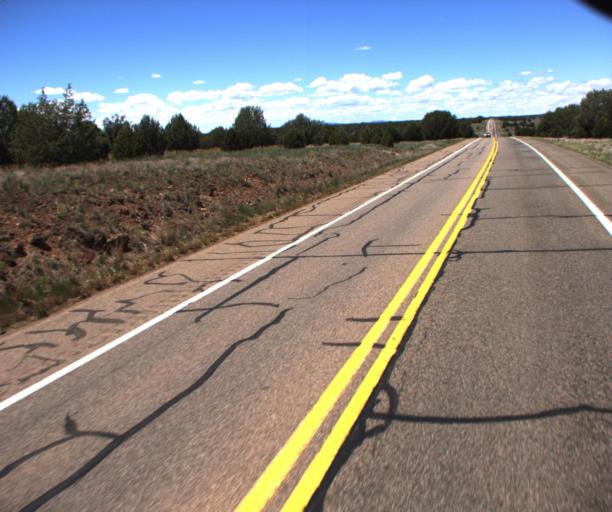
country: US
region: Arizona
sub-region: Yavapai County
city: Paulden
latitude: 35.1374
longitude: -112.4417
